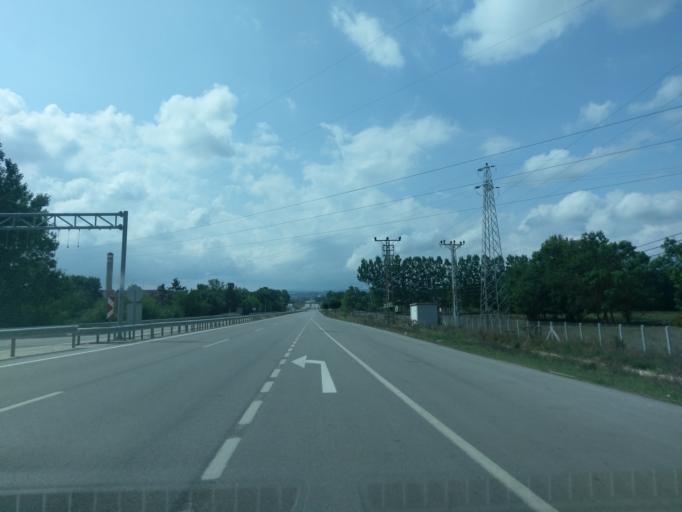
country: TR
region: Sinop
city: Kabali
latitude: 41.9254
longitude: 35.0815
